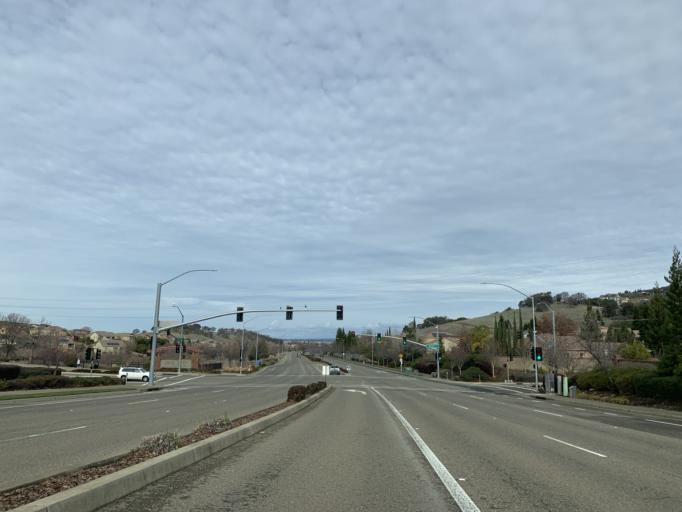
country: US
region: California
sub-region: El Dorado County
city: El Dorado Hills
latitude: 38.6549
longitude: -121.0921
